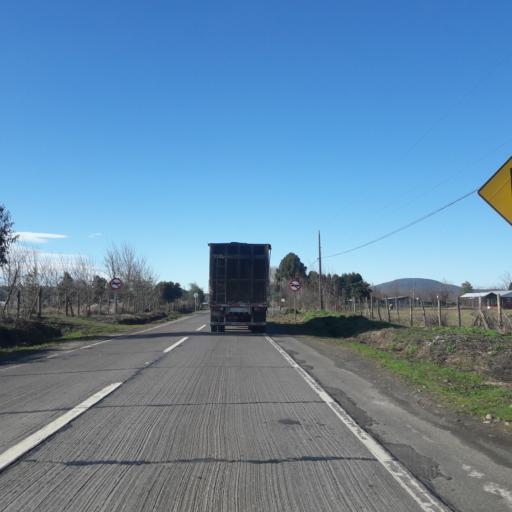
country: CL
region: Araucania
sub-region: Provincia de Malleco
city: Angol
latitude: -37.7813
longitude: -72.5333
